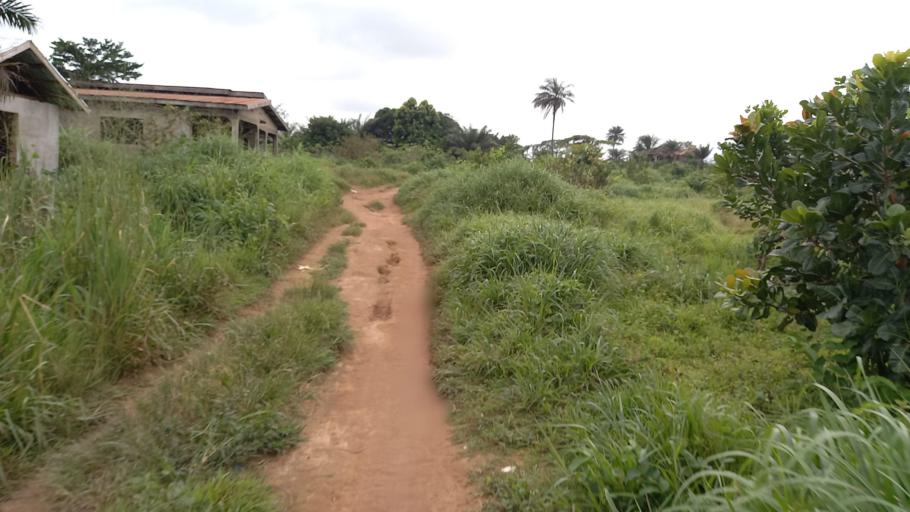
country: SL
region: Eastern Province
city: Kailahun
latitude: 8.2886
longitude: -10.5703
